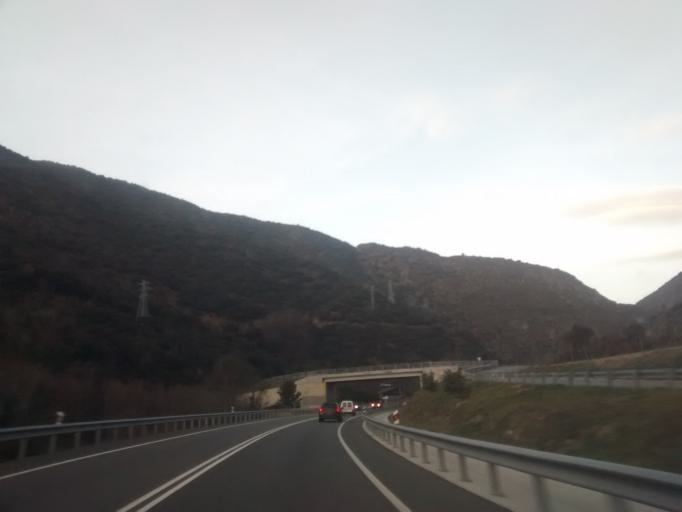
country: ES
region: Catalonia
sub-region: Provincia de Lleida
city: la Seu d'Urgell
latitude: 42.3936
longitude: 1.4614
